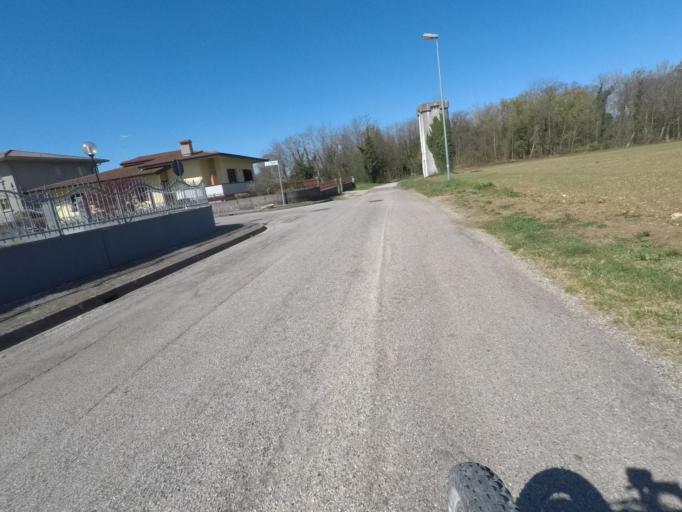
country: IT
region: Friuli Venezia Giulia
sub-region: Provincia di Udine
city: Moimacco
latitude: 46.0943
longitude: 13.3668
